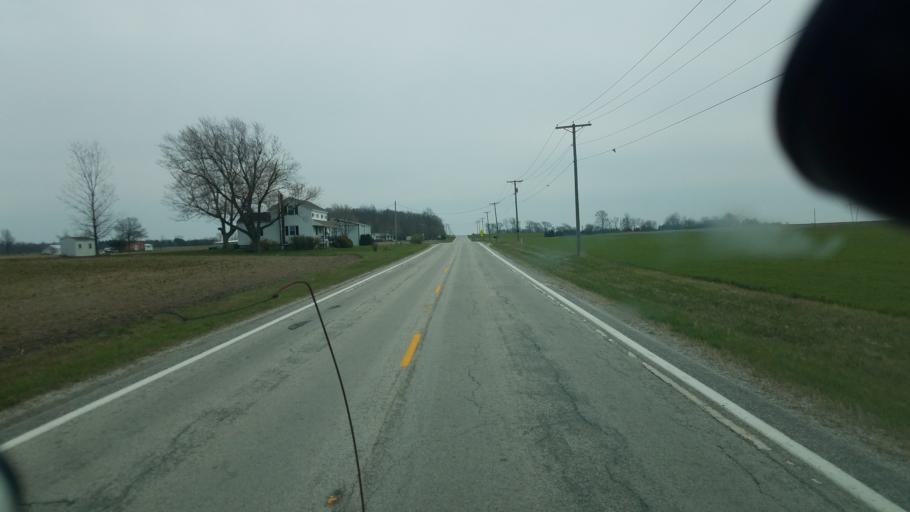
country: US
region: Ohio
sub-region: Wyandot County
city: Carey
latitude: 41.0175
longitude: -83.2881
